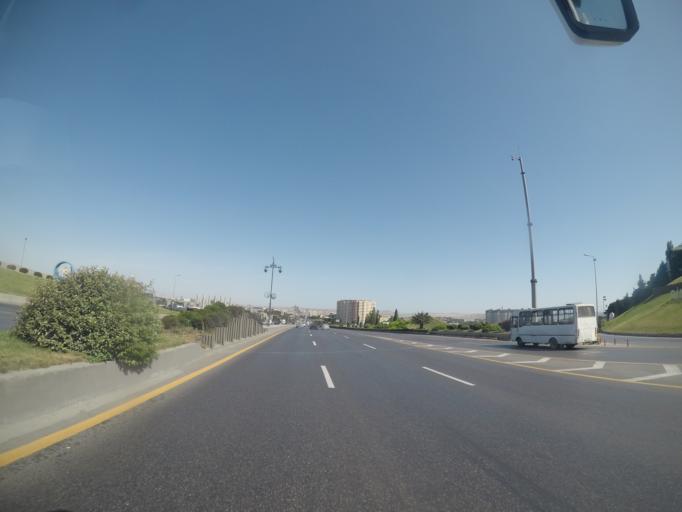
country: AZ
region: Baki
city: Bilajari
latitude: 40.4152
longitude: 49.8010
